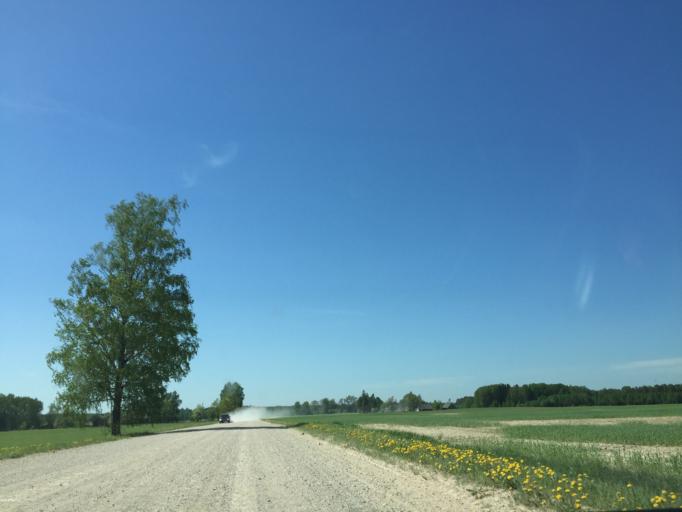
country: LV
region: Kegums
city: Kegums
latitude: 56.8567
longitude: 24.7391
